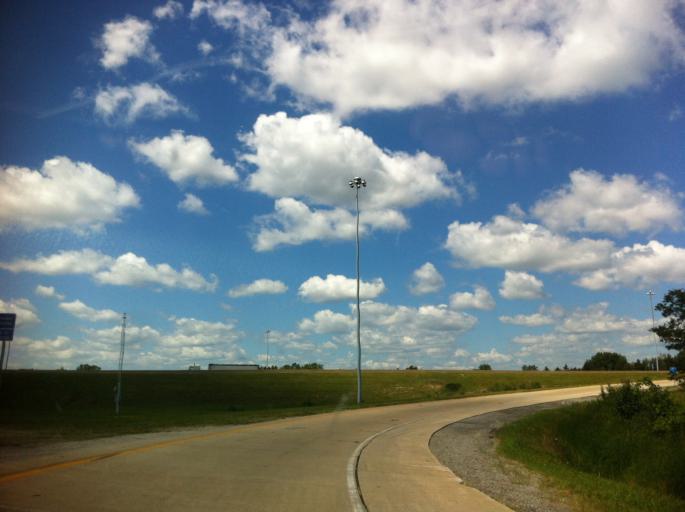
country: US
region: Ohio
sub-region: Wood County
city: Rossford
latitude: 41.5698
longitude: -83.5782
